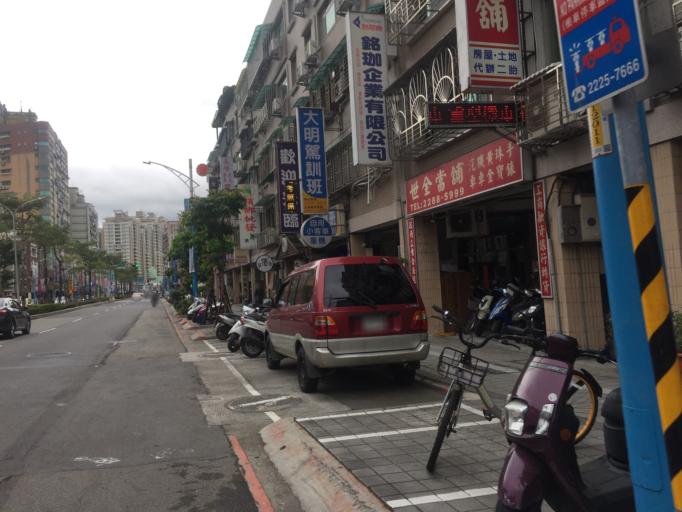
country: TW
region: Taipei
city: Taipei
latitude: 25.0877
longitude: 121.4706
